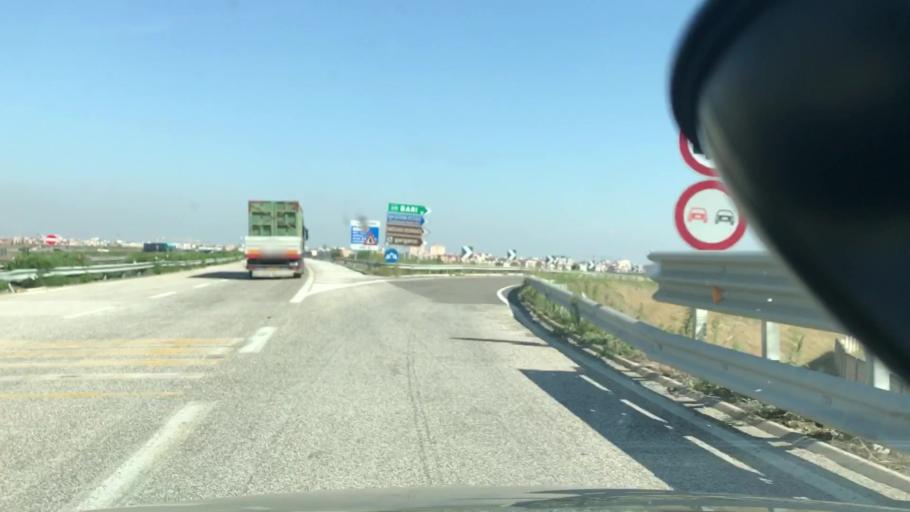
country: IT
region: Apulia
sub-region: Provincia di Foggia
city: Foggia
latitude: 41.4236
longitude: 15.5594
